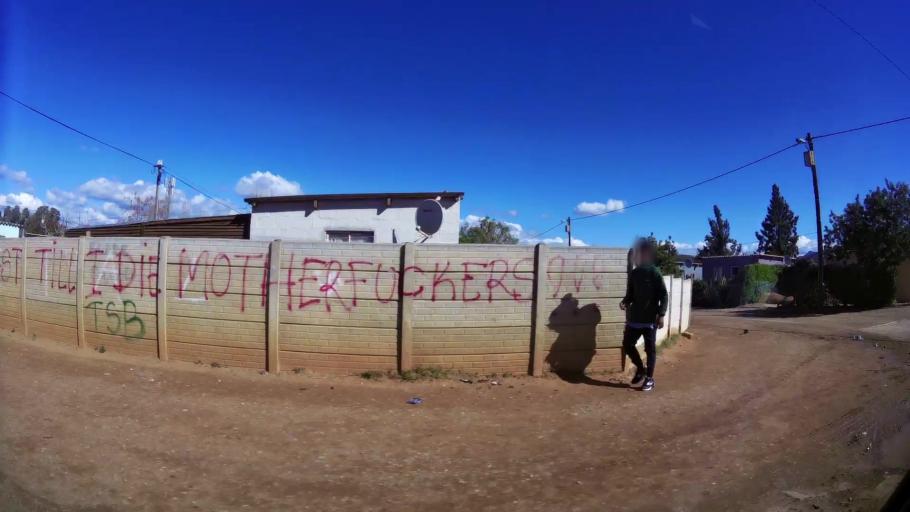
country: ZA
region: Western Cape
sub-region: Cape Winelands District Municipality
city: Ashton
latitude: -33.7922
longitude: 19.8816
